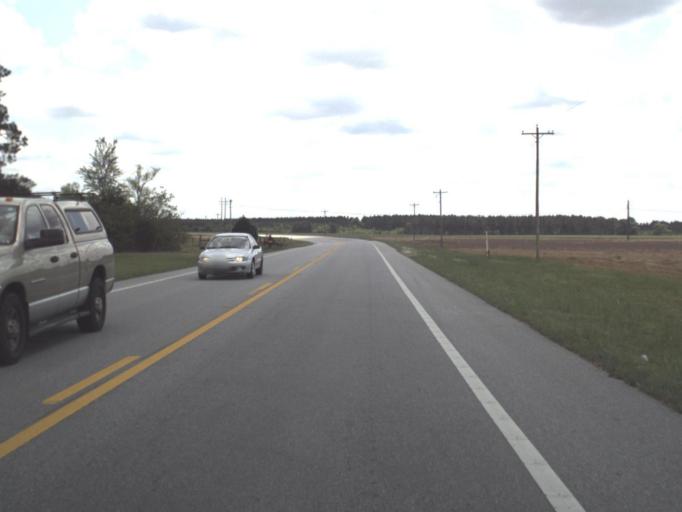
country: US
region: Alabama
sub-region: Escambia County
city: Atmore
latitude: 30.9355
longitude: -87.4879
